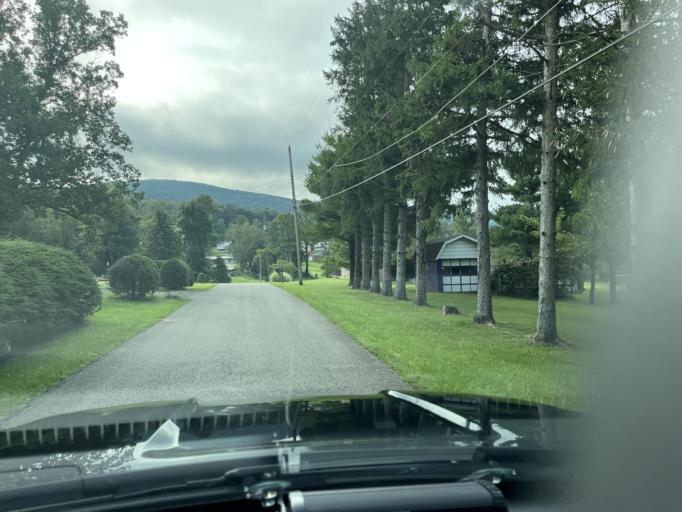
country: US
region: Pennsylvania
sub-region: Fayette County
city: Hopwood
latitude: 39.8684
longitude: -79.7019
